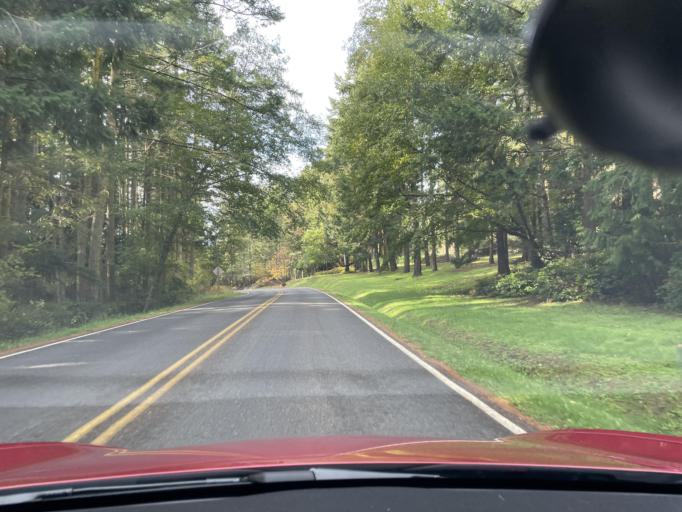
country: US
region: Washington
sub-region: San Juan County
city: Friday Harbor
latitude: 48.5290
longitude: -122.9882
